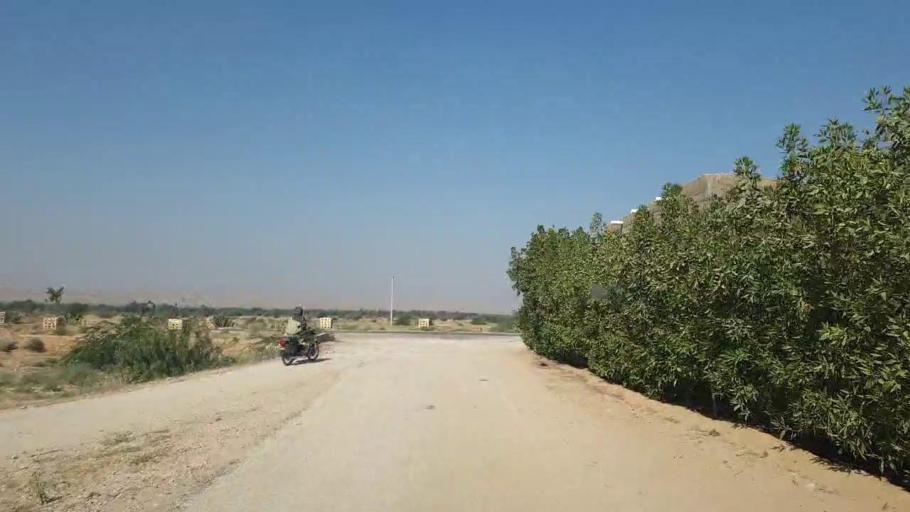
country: PK
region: Sindh
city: Jamshoro
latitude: 25.3697
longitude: 67.8407
